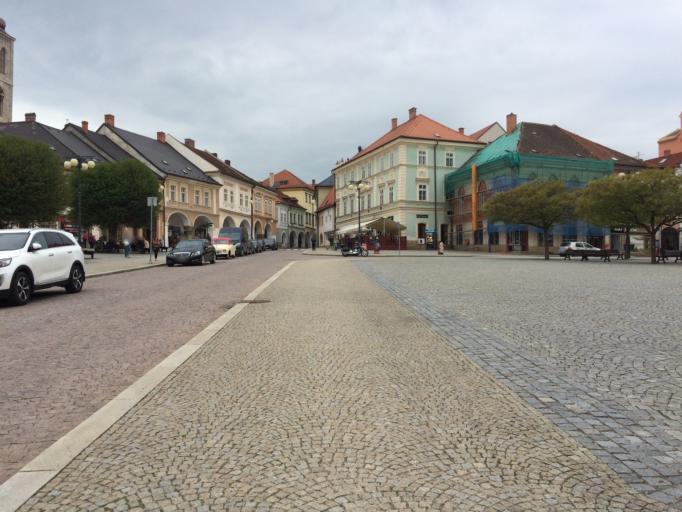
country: CZ
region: Central Bohemia
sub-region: Okres Kutna Hora
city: Kutna Hora
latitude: 49.9496
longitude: 15.2689
